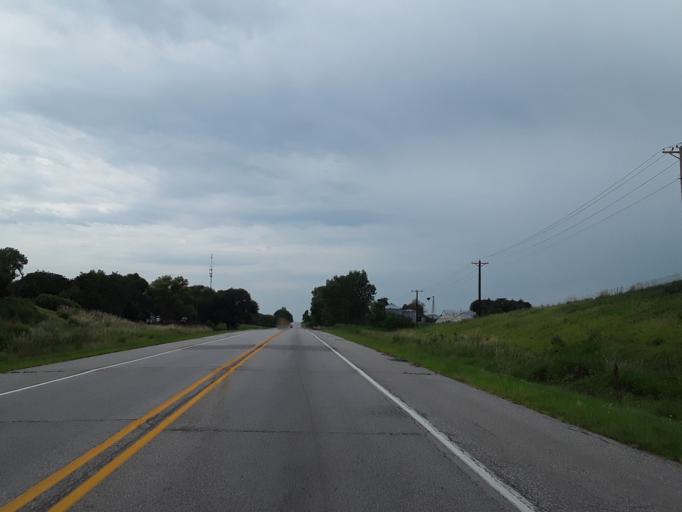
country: US
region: Nebraska
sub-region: Douglas County
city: Bennington
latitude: 41.3647
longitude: -96.0730
